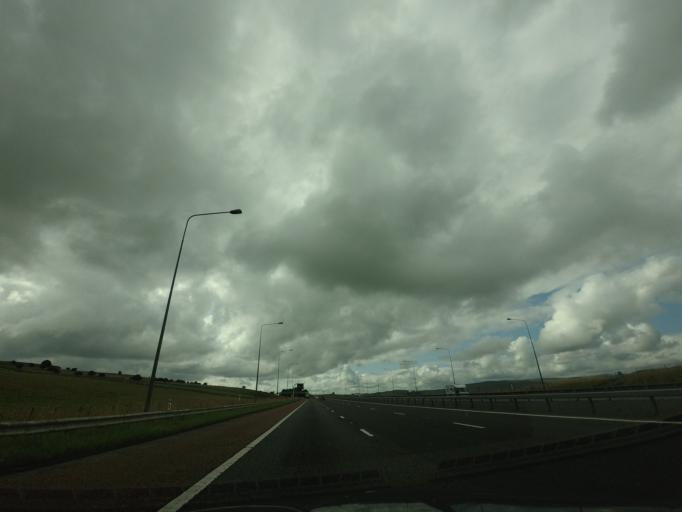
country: GB
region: England
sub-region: Cumbria
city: Penrith
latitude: 54.5256
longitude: -2.6588
